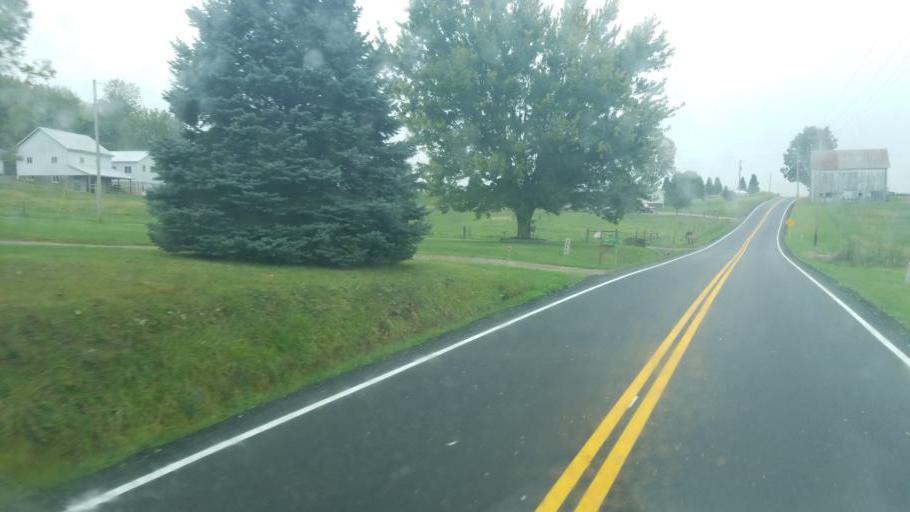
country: US
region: Ohio
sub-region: Wayne County
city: Shreve
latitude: 40.5842
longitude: -82.0672
